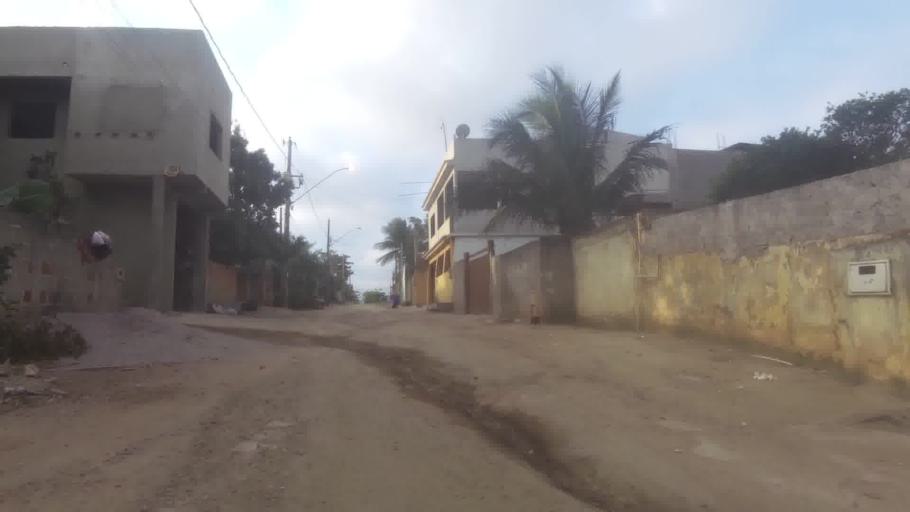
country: BR
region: Espirito Santo
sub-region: Itapemirim
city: Itapemirim
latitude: -21.0233
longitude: -40.8203
